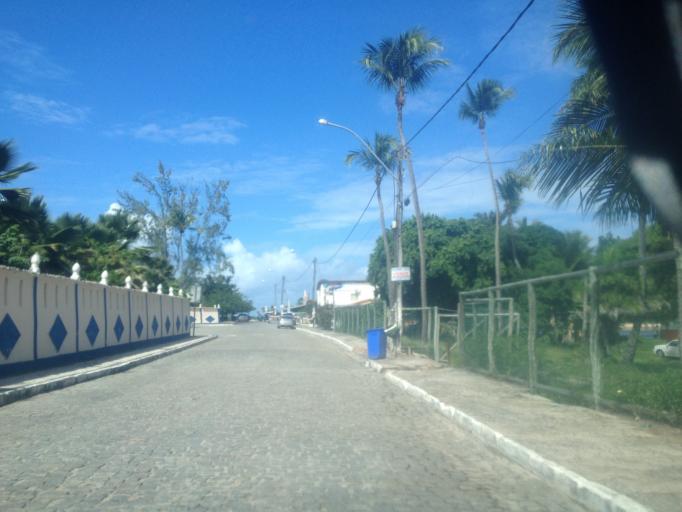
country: BR
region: Bahia
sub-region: Camacari
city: Camacari
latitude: -12.7057
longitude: -38.1312
